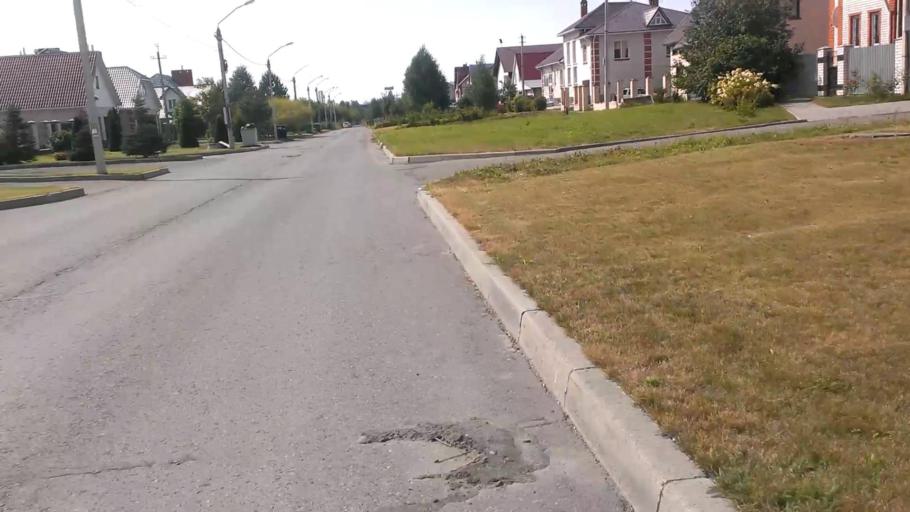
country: RU
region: Altai Krai
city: Novosilikatnyy
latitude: 53.3541
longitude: 83.6521
